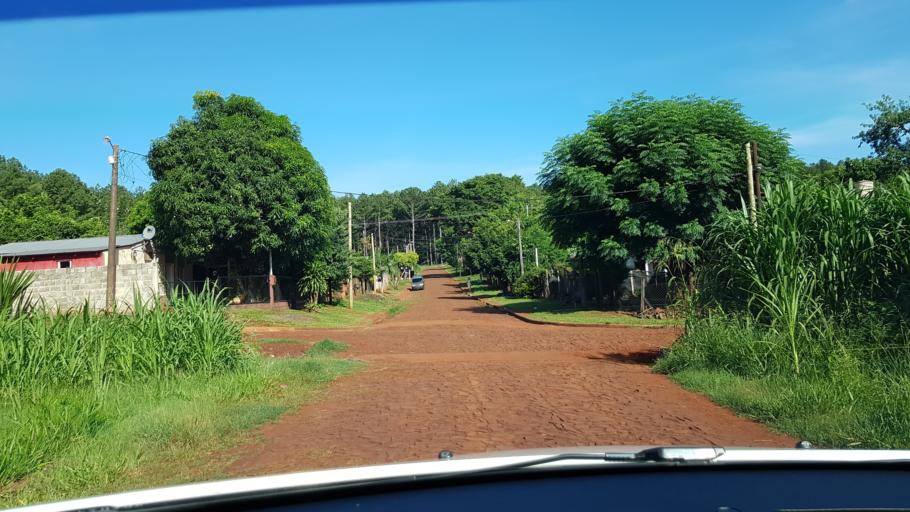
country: AR
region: Misiones
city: Puerto Libertad
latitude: -25.9139
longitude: -54.5797
